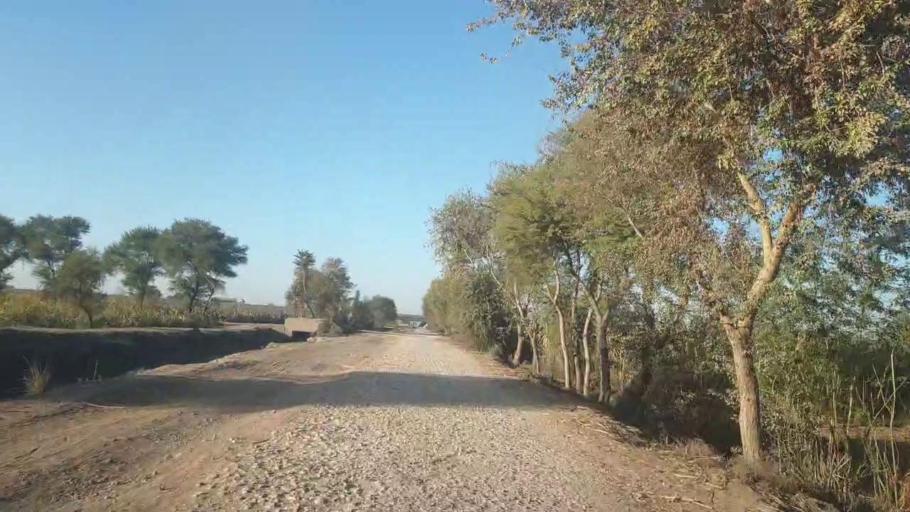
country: PK
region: Sindh
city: Ghotki
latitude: 28.0043
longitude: 69.2701
